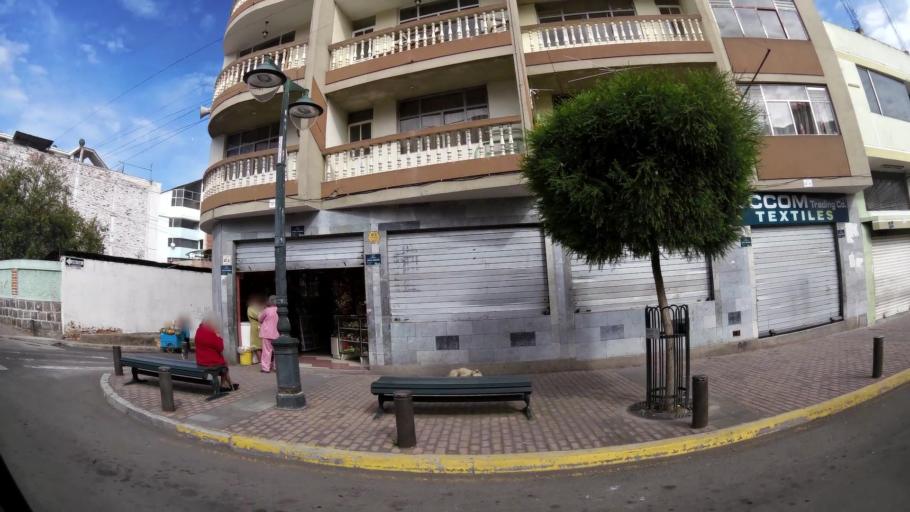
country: EC
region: Tungurahua
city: Ambato
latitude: -1.2459
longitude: -78.6375
